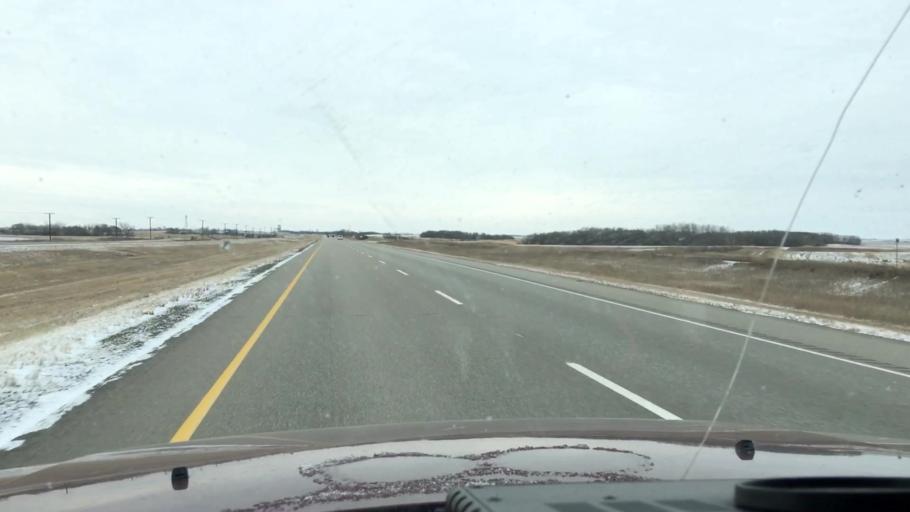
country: CA
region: Saskatchewan
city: Watrous
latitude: 51.3914
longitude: -106.1670
